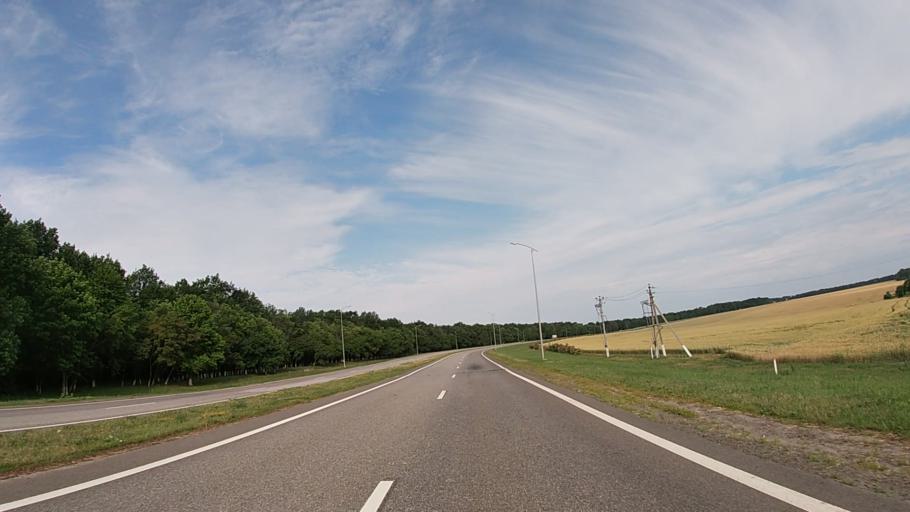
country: RU
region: Belgorod
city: Borisovka
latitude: 50.7513
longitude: 35.9762
